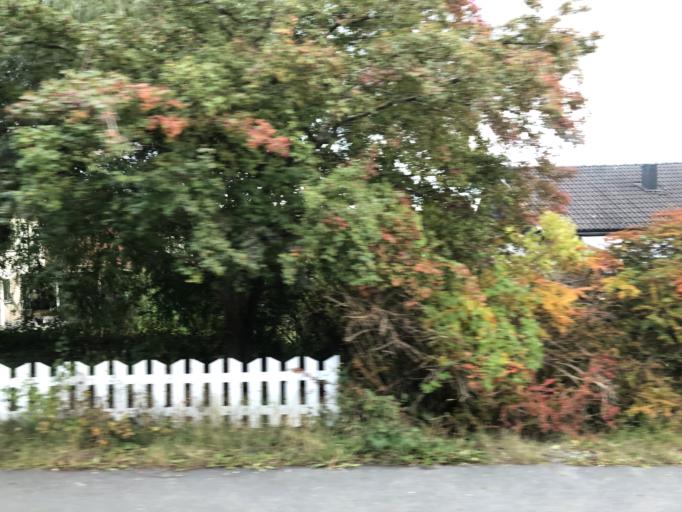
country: SE
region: Stockholm
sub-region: Jarfalla Kommun
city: Jakobsberg
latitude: 59.4237
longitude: 17.8082
